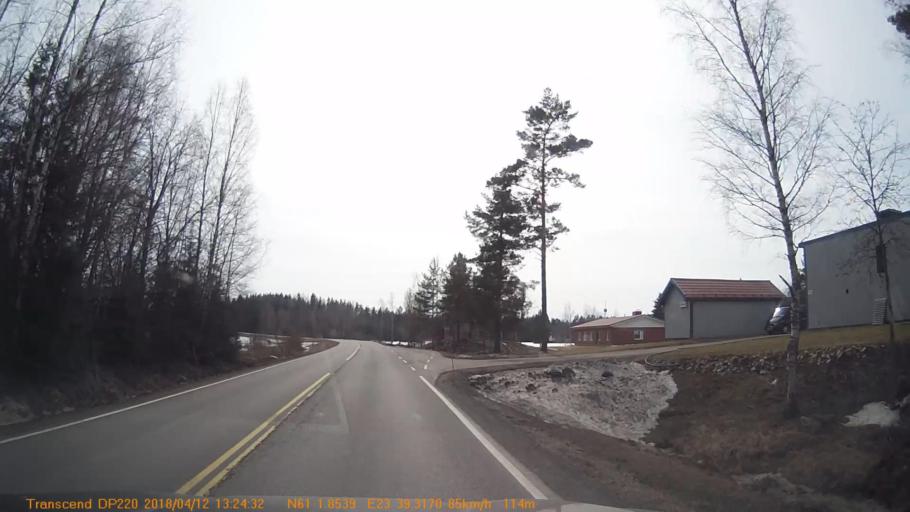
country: FI
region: Pirkanmaa
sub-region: Etelae-Pirkanmaa
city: Kylmaekoski
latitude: 61.0296
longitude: 23.6549
